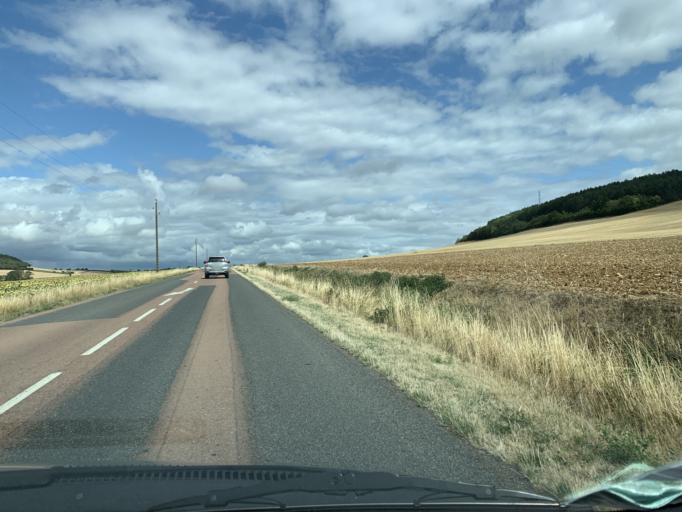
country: FR
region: Bourgogne
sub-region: Departement de la Nievre
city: Varzy
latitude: 47.3659
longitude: 3.4119
